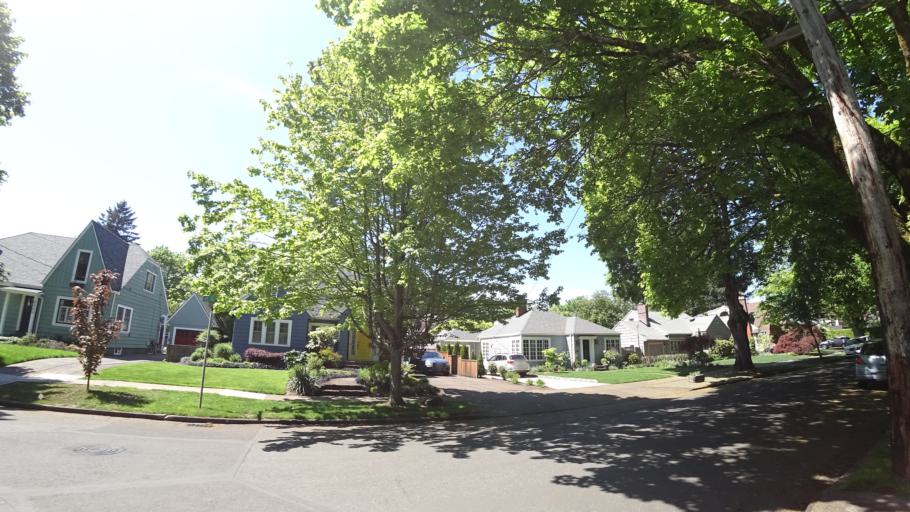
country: US
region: Oregon
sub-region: Clackamas County
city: Milwaukie
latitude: 45.4657
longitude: -122.6262
